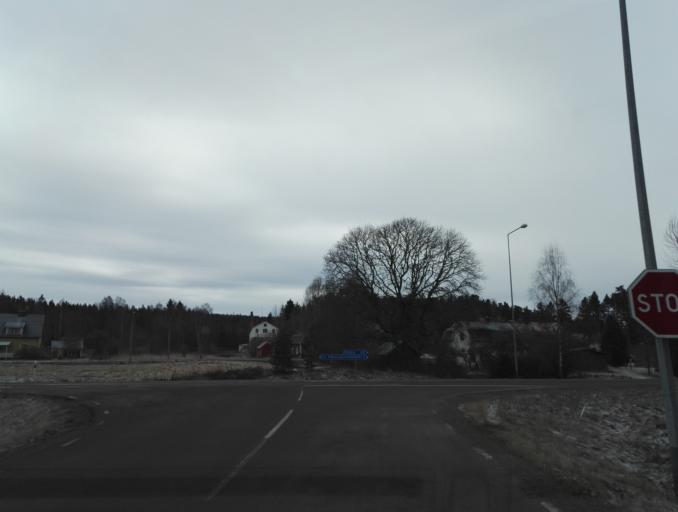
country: SE
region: Kalmar
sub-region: Hultsfreds Kommun
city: Virserum
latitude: 57.3441
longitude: 15.6063
